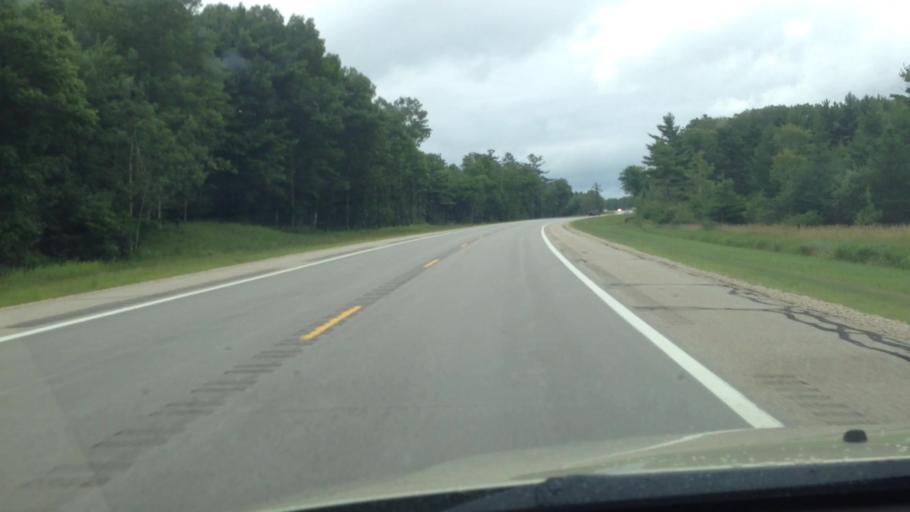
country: US
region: Michigan
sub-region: Schoolcraft County
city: Manistique
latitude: 45.9108
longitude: -86.4555
